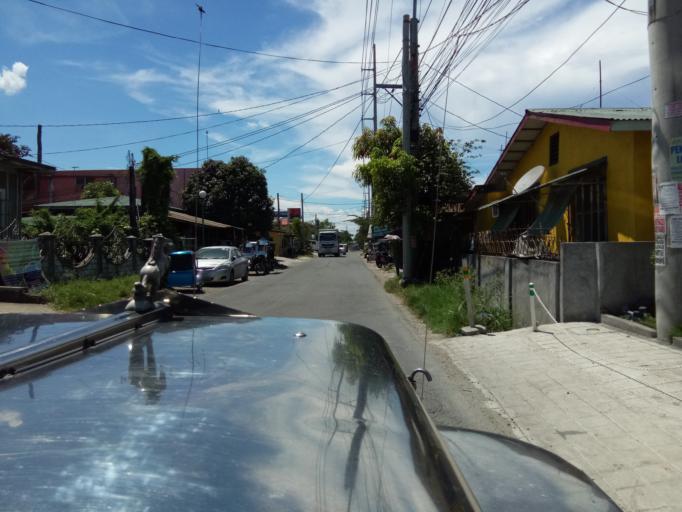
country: PH
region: Calabarzon
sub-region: Province of Cavite
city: Pasong Kawayan Primero
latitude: 14.3588
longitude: 120.8975
